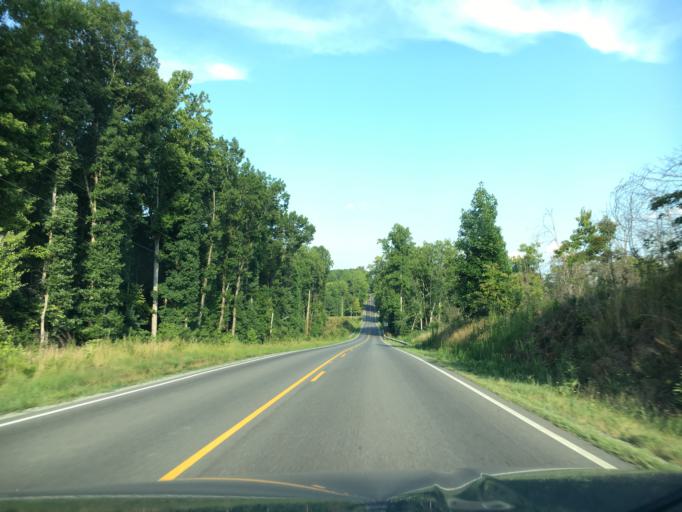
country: US
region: Virginia
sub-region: Franklin County
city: Union Hall
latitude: 36.9738
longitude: -79.6092
